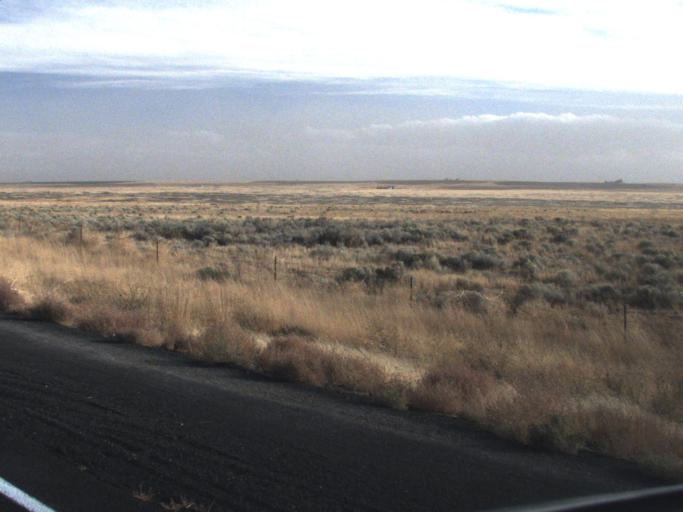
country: US
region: Washington
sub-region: Grant County
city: Warden
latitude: 47.3491
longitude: -118.9319
